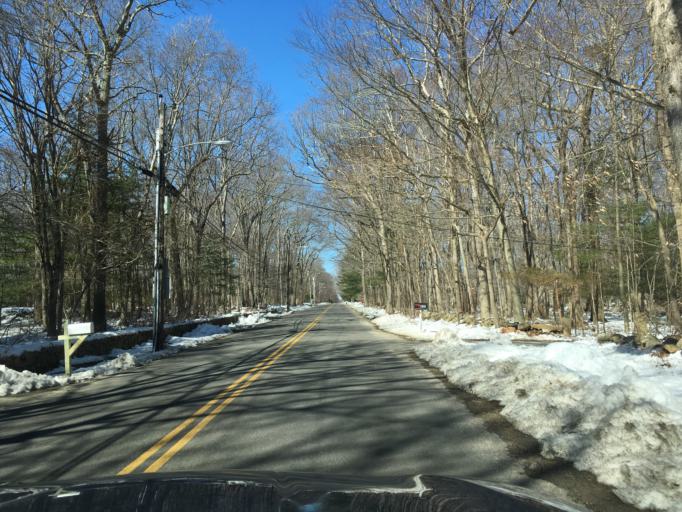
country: US
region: Rhode Island
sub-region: Washington County
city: Exeter
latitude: 41.6075
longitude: -71.5346
